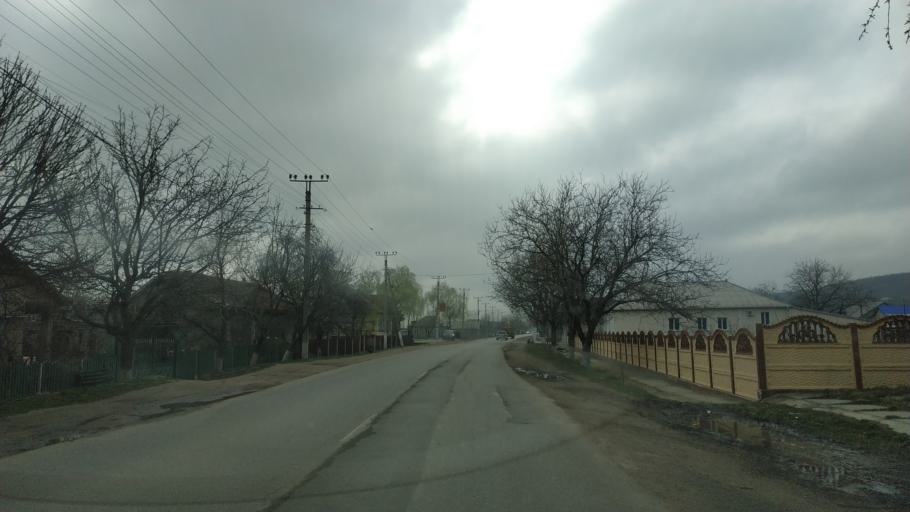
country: MD
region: Cimislia
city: Cimislia
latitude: 46.5142
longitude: 28.7999
